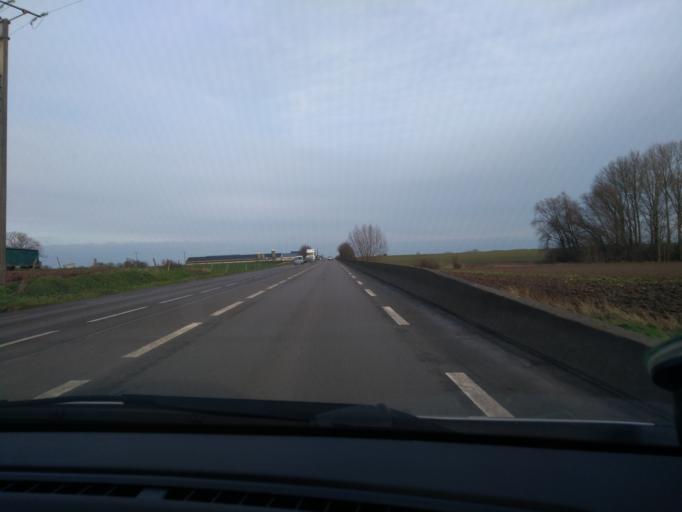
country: FR
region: Nord-Pas-de-Calais
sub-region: Departement du Nord
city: Maubeuge
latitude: 50.3205
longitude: 3.9762
